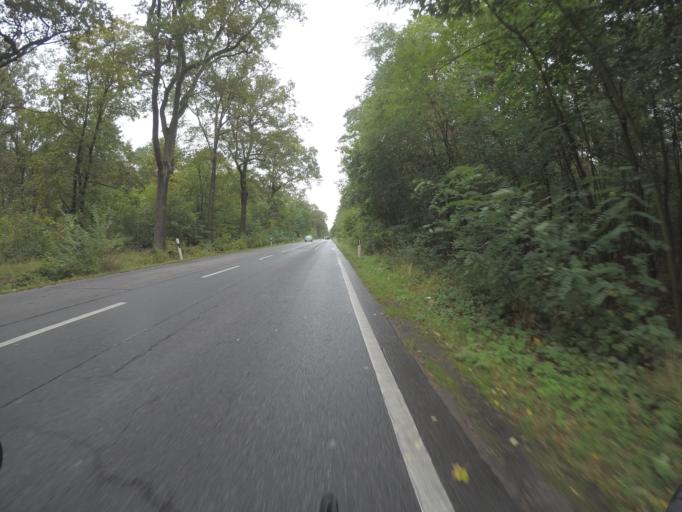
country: DE
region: Berlin
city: Buch
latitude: 52.6365
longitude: 13.4713
